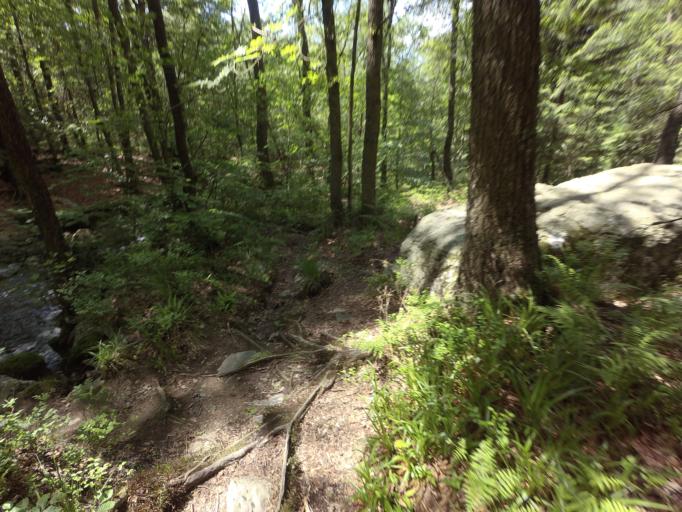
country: BE
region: Wallonia
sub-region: Province de Liege
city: Jalhay
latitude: 50.5213
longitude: 5.9974
